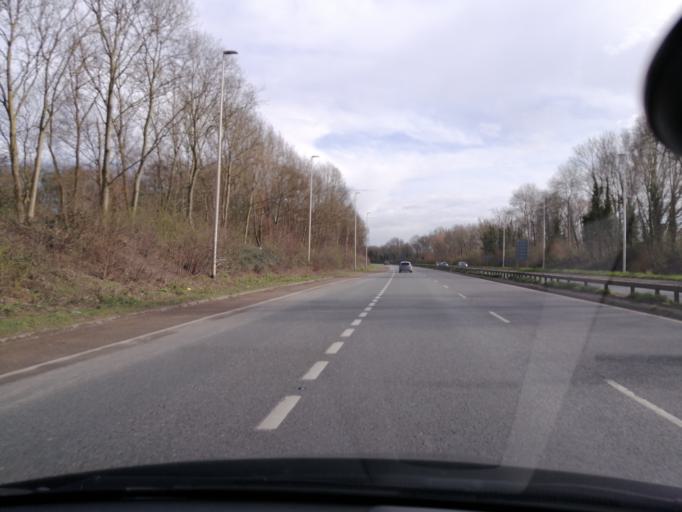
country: GB
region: England
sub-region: Peterborough
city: Eye
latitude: 52.6017
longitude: -0.2236
